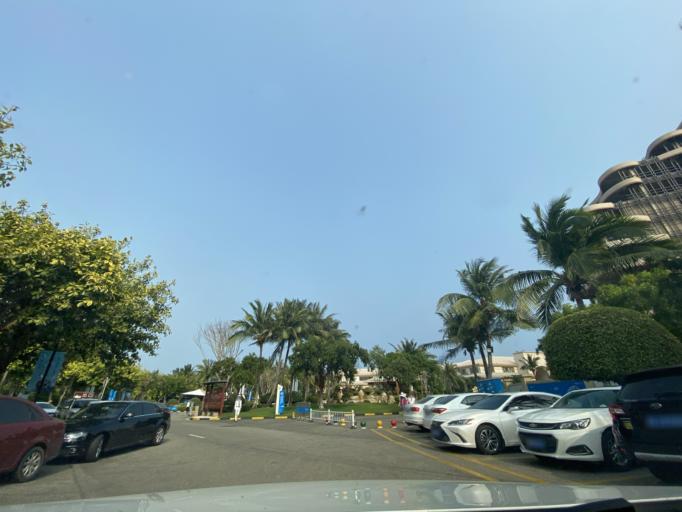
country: CN
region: Hainan
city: Yingzhou
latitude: 18.3940
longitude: 109.8576
